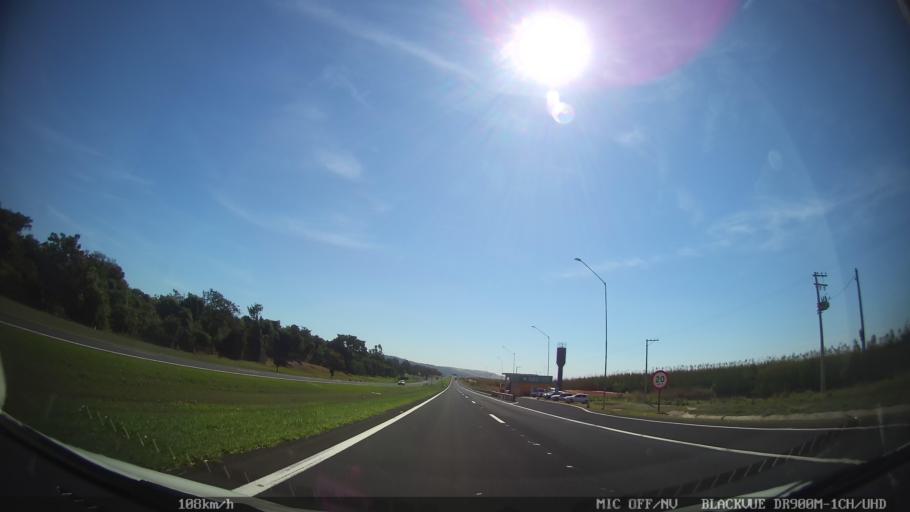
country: BR
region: Sao Paulo
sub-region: Sao Simao
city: Sao Simao
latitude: -21.5450
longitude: -47.6392
